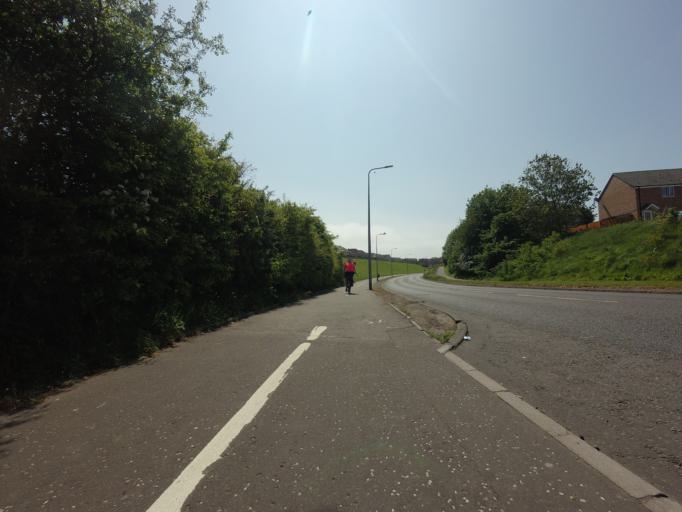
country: GB
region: Scotland
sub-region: Fife
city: Townhill
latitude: 56.0645
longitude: -3.4143
